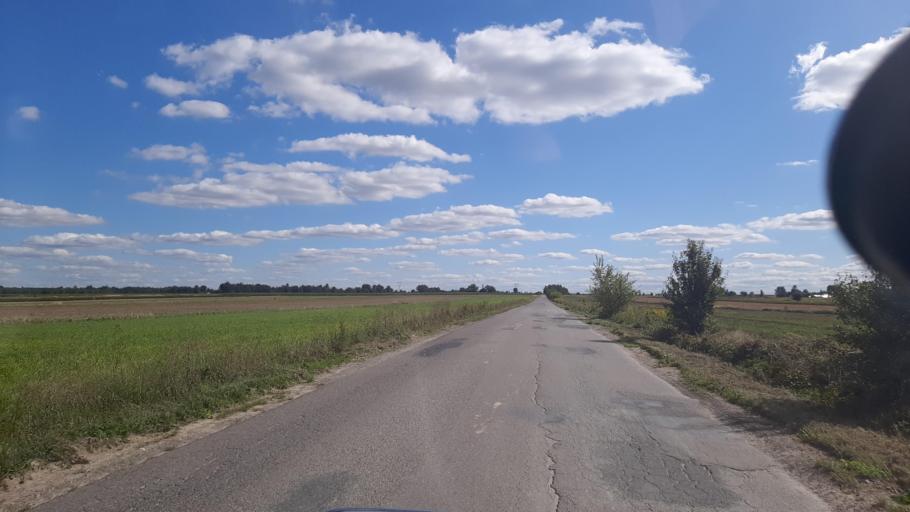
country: PL
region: Lublin Voivodeship
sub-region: Powiat pulawski
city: Markuszow
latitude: 51.4068
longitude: 22.2332
